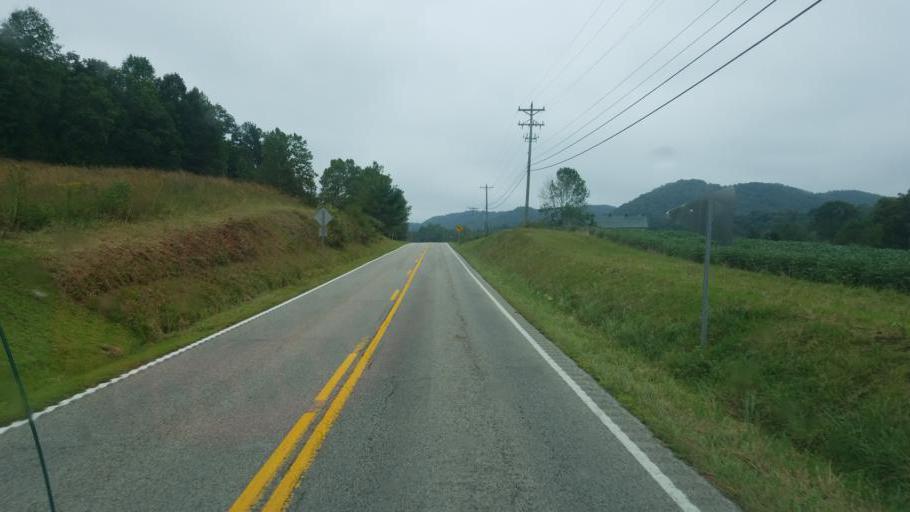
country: US
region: Kentucky
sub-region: Rowan County
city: Morehead
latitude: 38.2642
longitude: -83.4337
